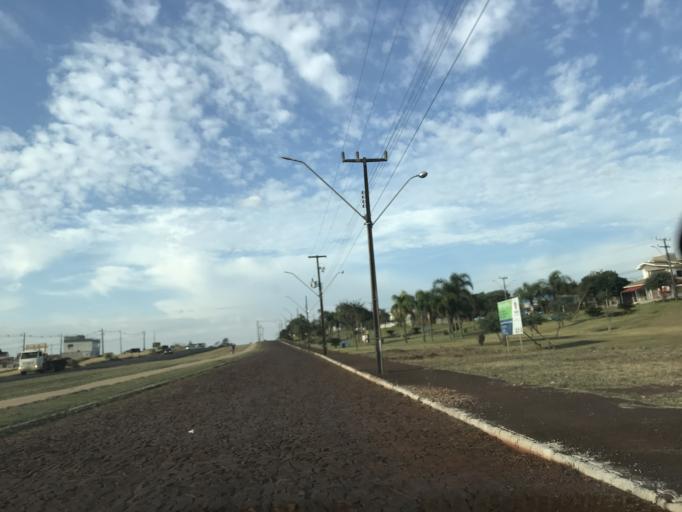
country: BR
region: Parana
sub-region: Cascavel
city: Cascavel
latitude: -25.0486
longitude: -53.6140
